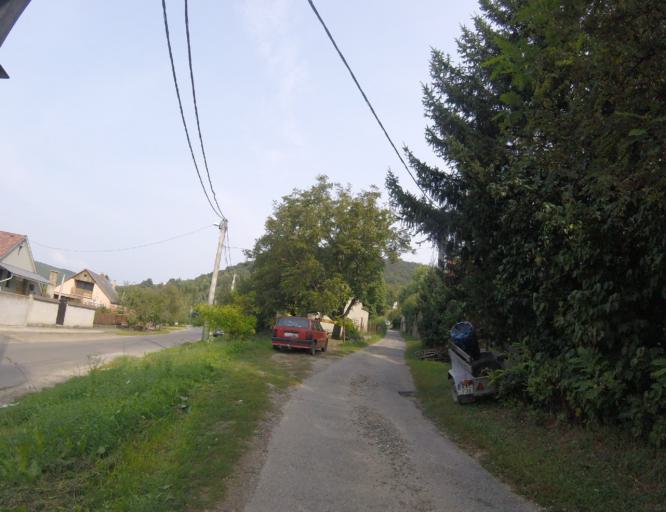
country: HU
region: Pest
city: Veroce
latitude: 47.8313
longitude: 19.0408
